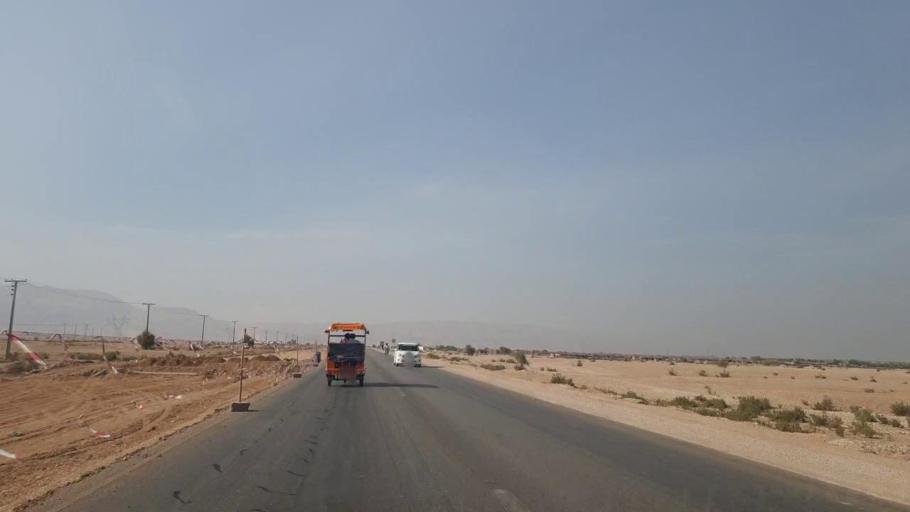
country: PK
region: Sindh
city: Sehwan
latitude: 26.1973
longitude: 67.9433
